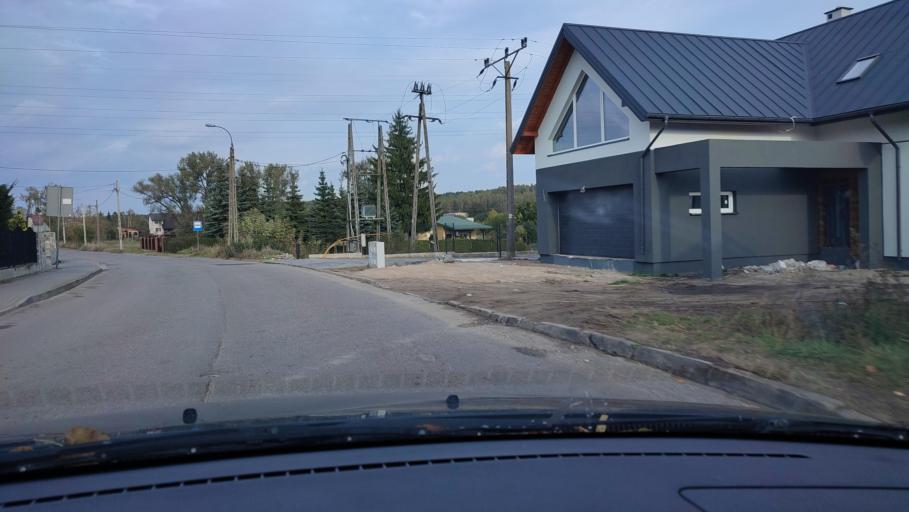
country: PL
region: Masovian Voivodeship
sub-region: Powiat mlawski
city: Mlawa
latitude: 53.1324
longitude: 20.3621
